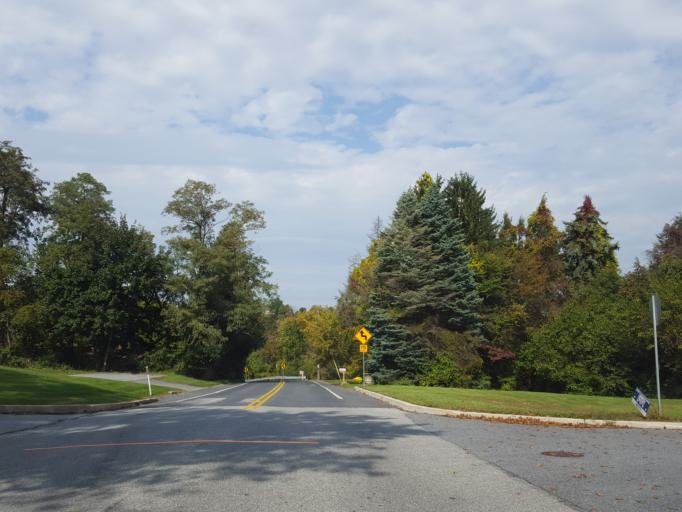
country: US
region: Pennsylvania
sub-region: York County
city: Spry
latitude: 39.9185
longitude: -76.6776
